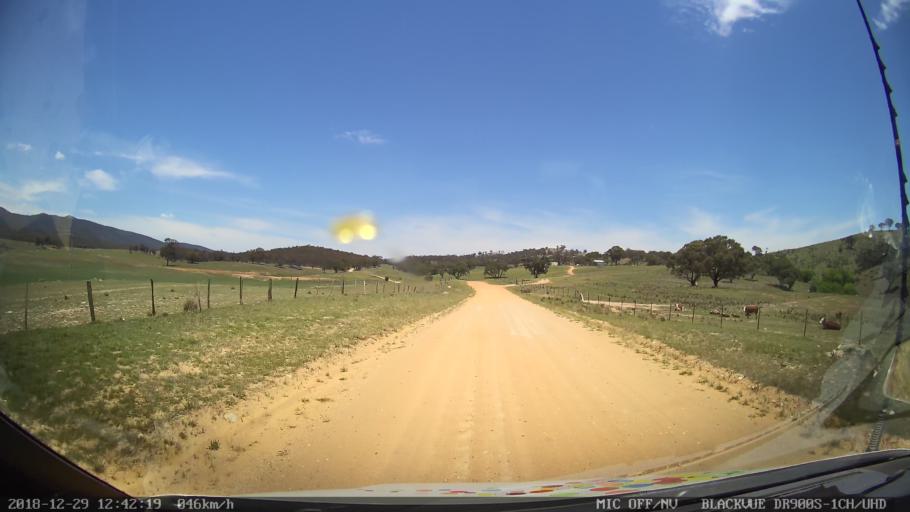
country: AU
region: Australian Capital Territory
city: Macarthur
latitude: -35.6115
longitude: 149.2197
